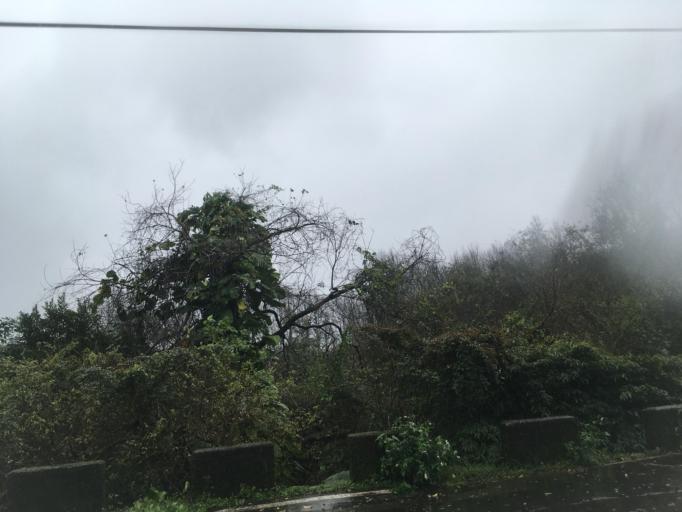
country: TW
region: Taiwan
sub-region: Keelung
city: Keelung
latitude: 25.0657
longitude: 121.9017
